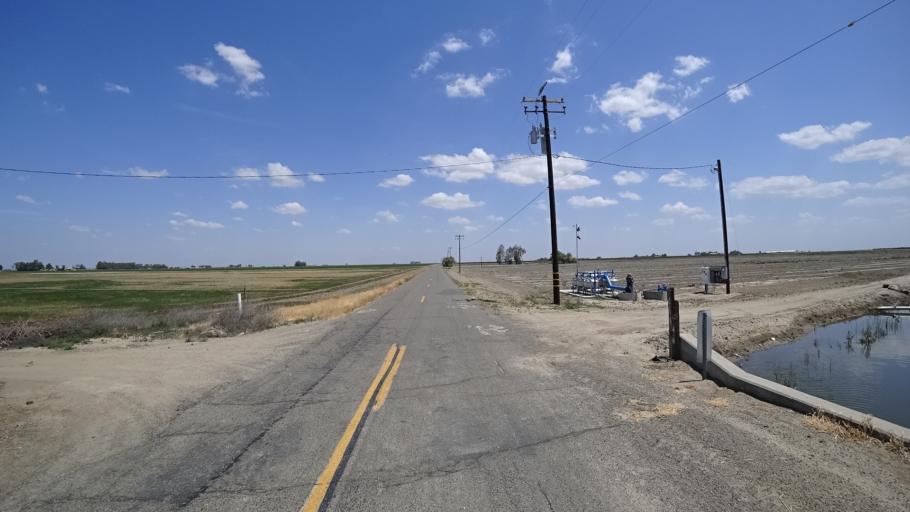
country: US
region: California
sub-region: Kings County
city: Stratford
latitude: 36.1821
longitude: -119.8152
